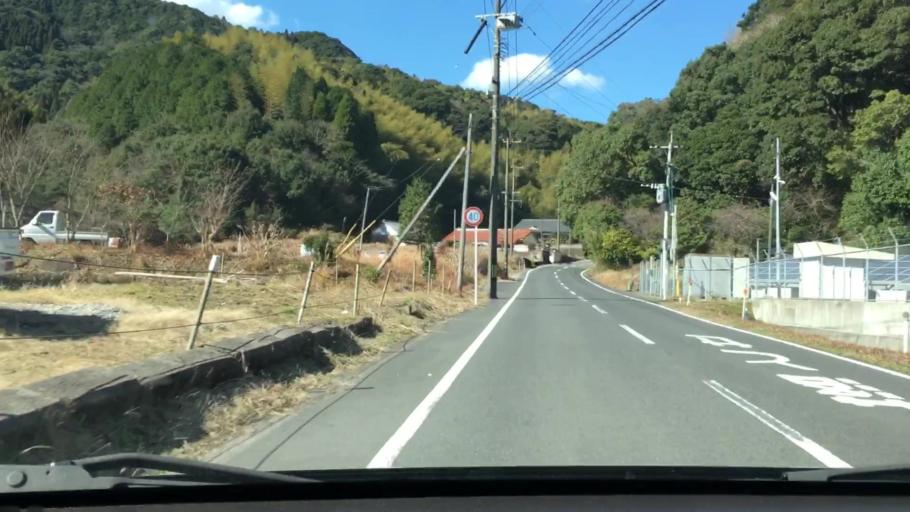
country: JP
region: Kagoshima
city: Ijuin
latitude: 31.7098
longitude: 130.4398
